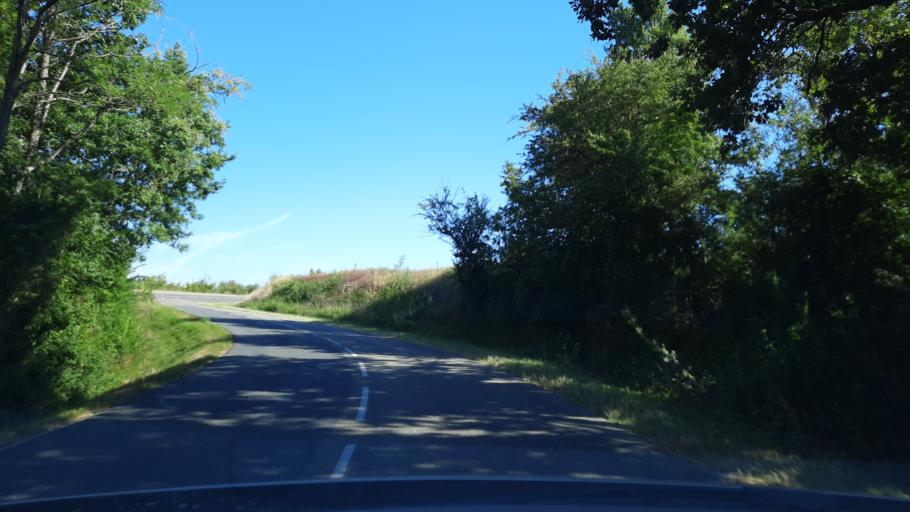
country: FR
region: Midi-Pyrenees
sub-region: Departement du Tarn-et-Garonne
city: Realville
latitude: 44.1896
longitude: 1.4641
